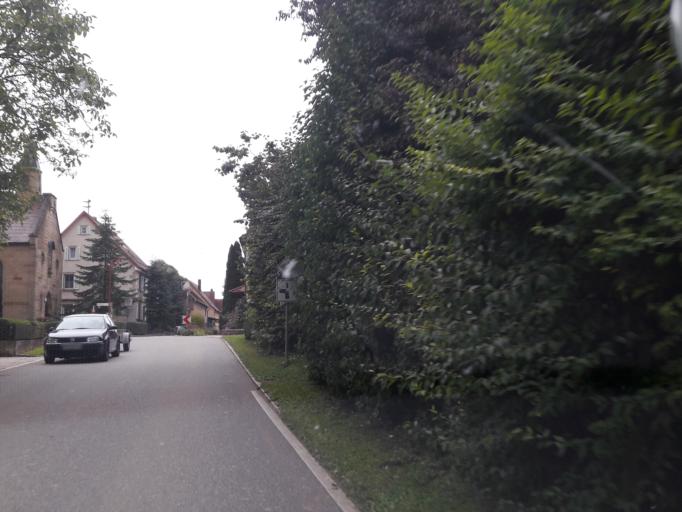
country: DE
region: Baden-Wuerttemberg
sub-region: Regierungsbezirk Stuttgart
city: Neuenstadt am Kocher
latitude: 49.2278
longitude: 9.3043
